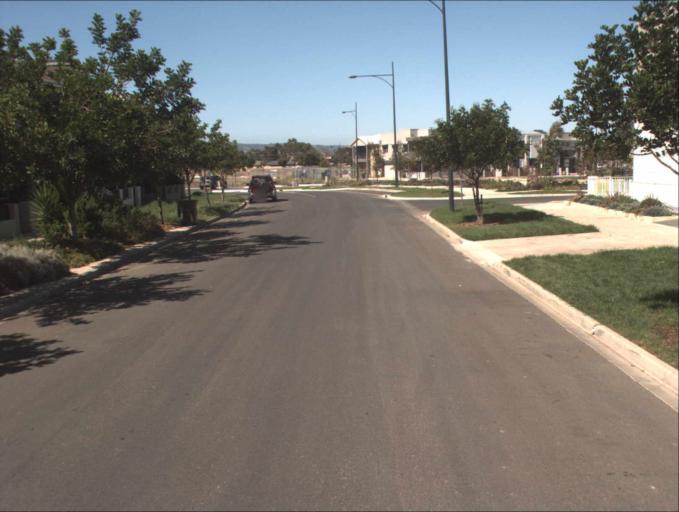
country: AU
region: South Australia
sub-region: Port Adelaide Enfield
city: Klemzig
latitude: -34.8613
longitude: 138.6280
